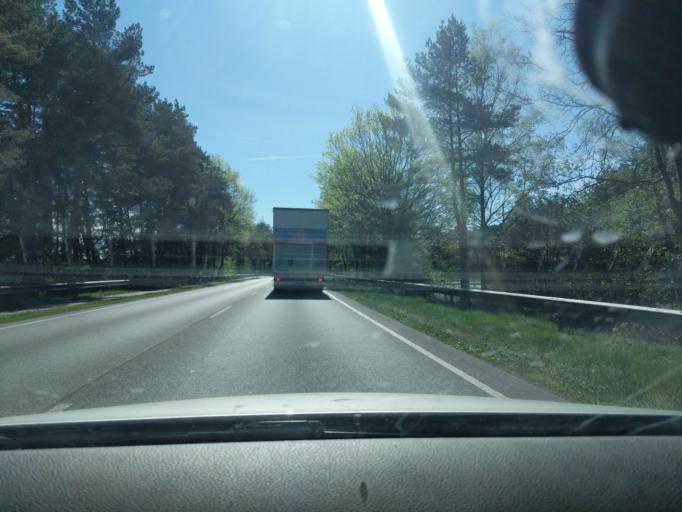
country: DE
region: Lower Saxony
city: Buxtehude
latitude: 53.4571
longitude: 9.7241
